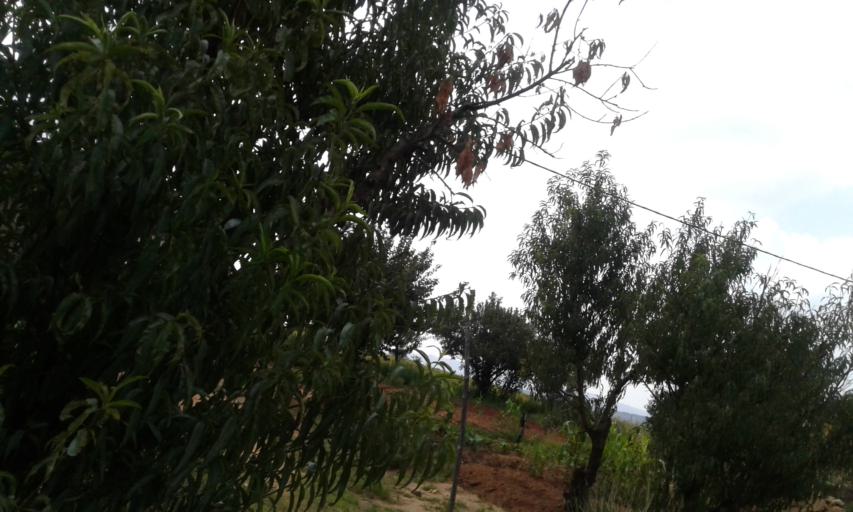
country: LS
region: Maseru
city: Maseru
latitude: -29.4312
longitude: 27.5746
